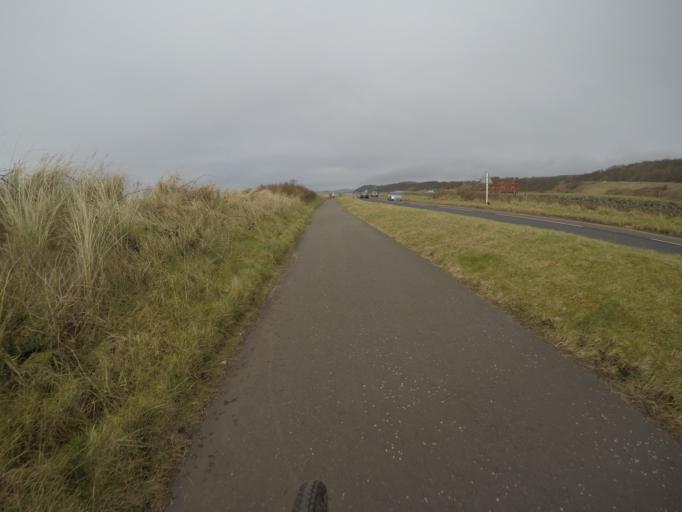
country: GB
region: Scotland
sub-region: North Ayrshire
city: Ardrossan
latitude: 55.6569
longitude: -4.8286
